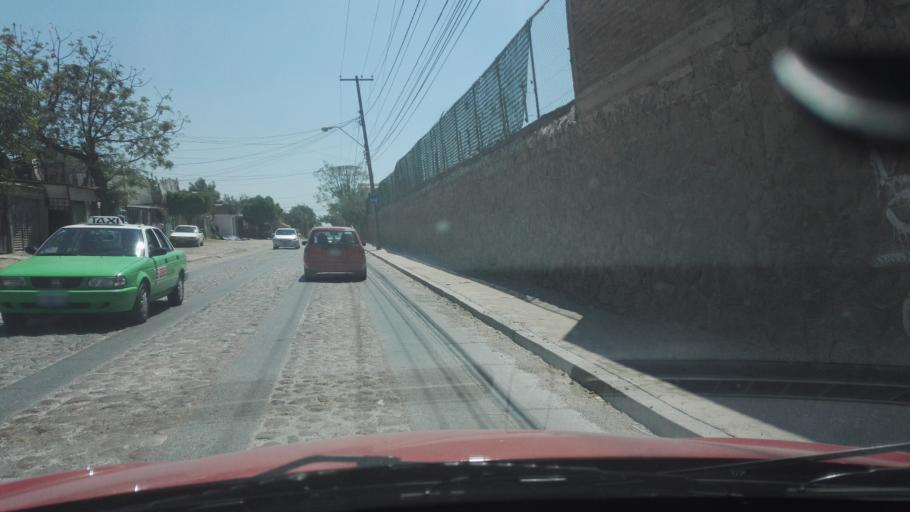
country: MX
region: Guanajuato
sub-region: Leon
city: Fraccionamiento Paraiso Real
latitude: 21.0952
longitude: -101.6012
